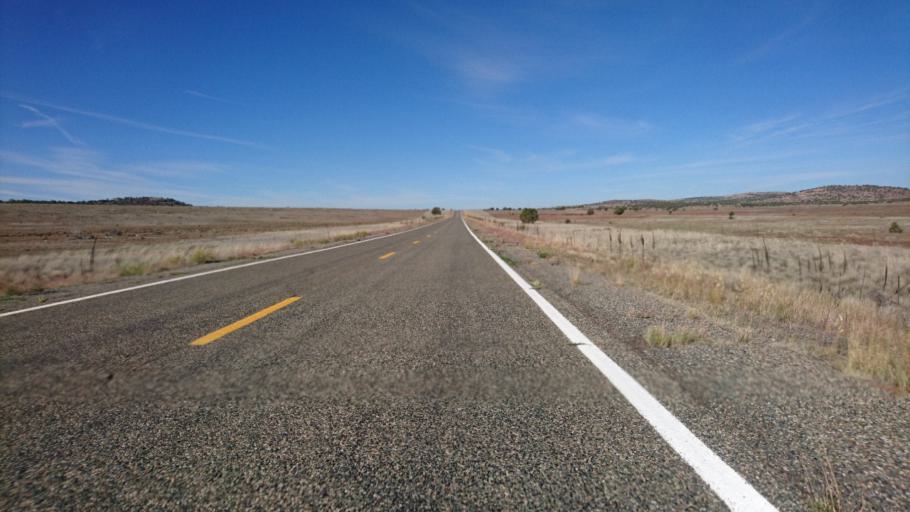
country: US
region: Arizona
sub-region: Yavapai County
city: Paulden
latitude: 35.2847
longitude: -112.7195
